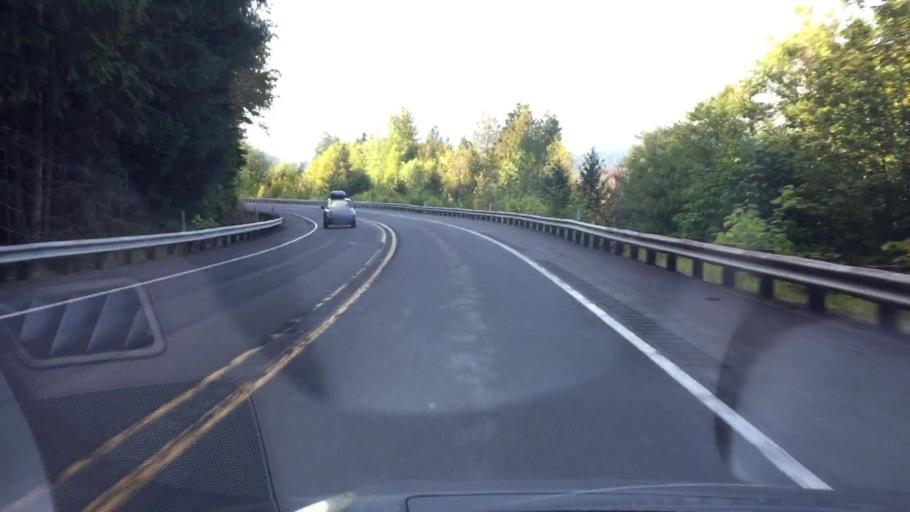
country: US
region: Washington
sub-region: Lewis County
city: Morton
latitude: 46.5201
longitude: -122.2192
